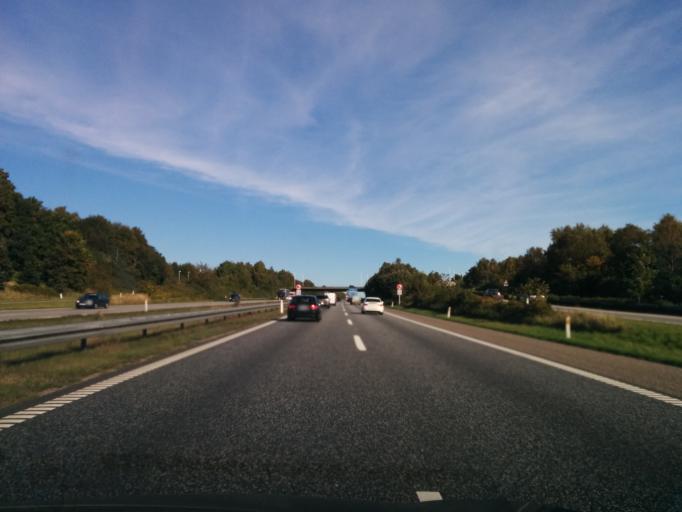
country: DK
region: Central Jutland
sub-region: Skanderborg Kommune
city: Stilling
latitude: 56.0647
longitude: 9.9735
